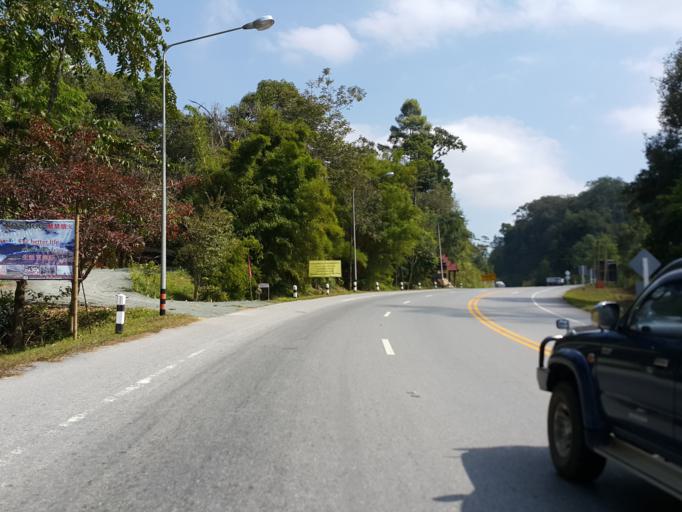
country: TH
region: Lampang
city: Wang Nuea
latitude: 19.0669
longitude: 99.3767
